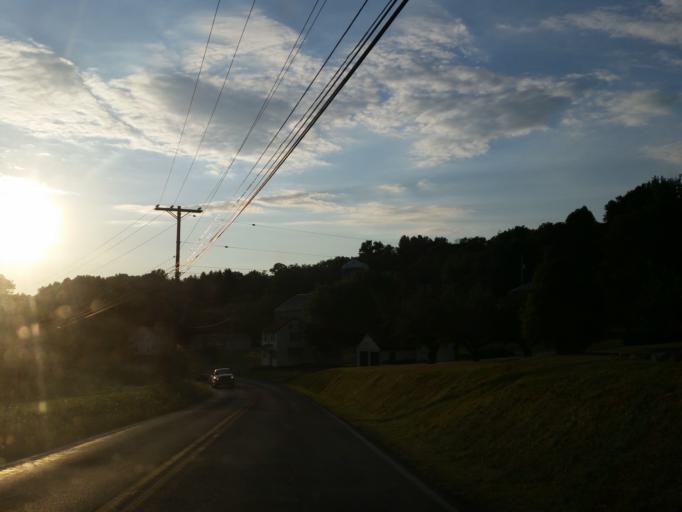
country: US
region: Pennsylvania
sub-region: Berks County
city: Alleghenyville
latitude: 40.2463
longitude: -76.0081
